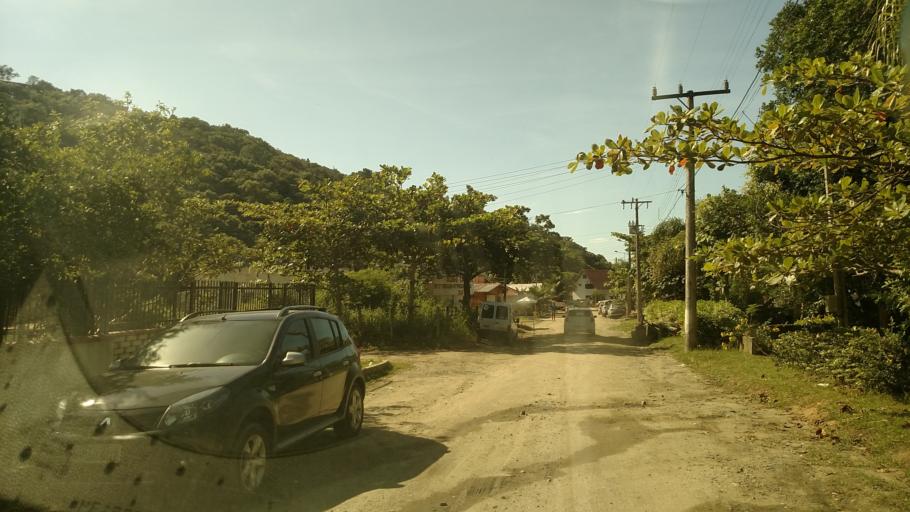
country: BR
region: Santa Catarina
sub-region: Porto Belo
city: Porto Belo
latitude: -27.2145
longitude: -48.5096
